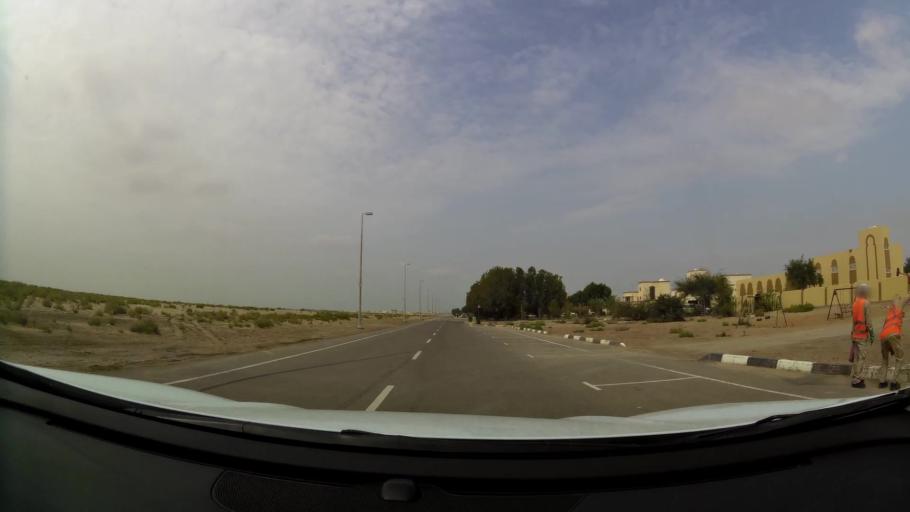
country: AE
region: Abu Dhabi
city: Abu Dhabi
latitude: 24.6312
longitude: 54.6870
